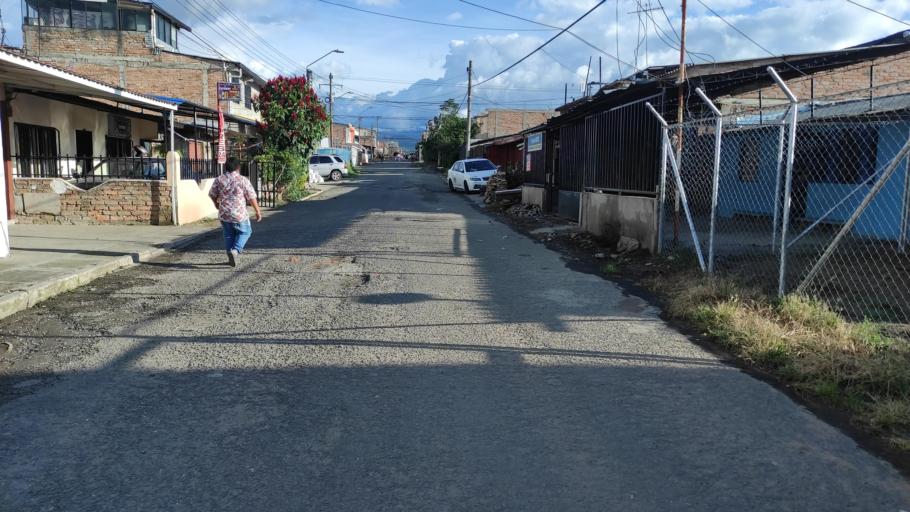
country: CO
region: Cauca
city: Popayan
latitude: 2.4902
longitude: -76.5679
